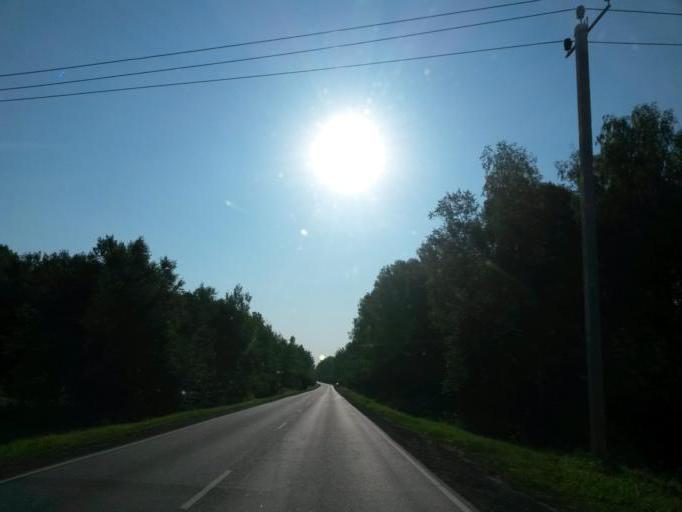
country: RU
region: Moskovskaya
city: Melikhovo
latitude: 55.1884
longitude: 37.7177
